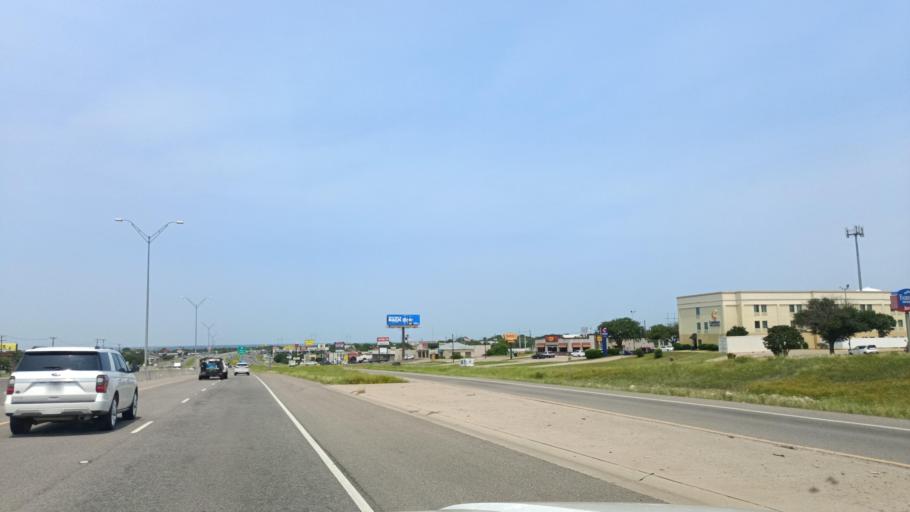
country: US
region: Texas
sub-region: Bell County
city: Temple
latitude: 31.0738
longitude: -97.3691
